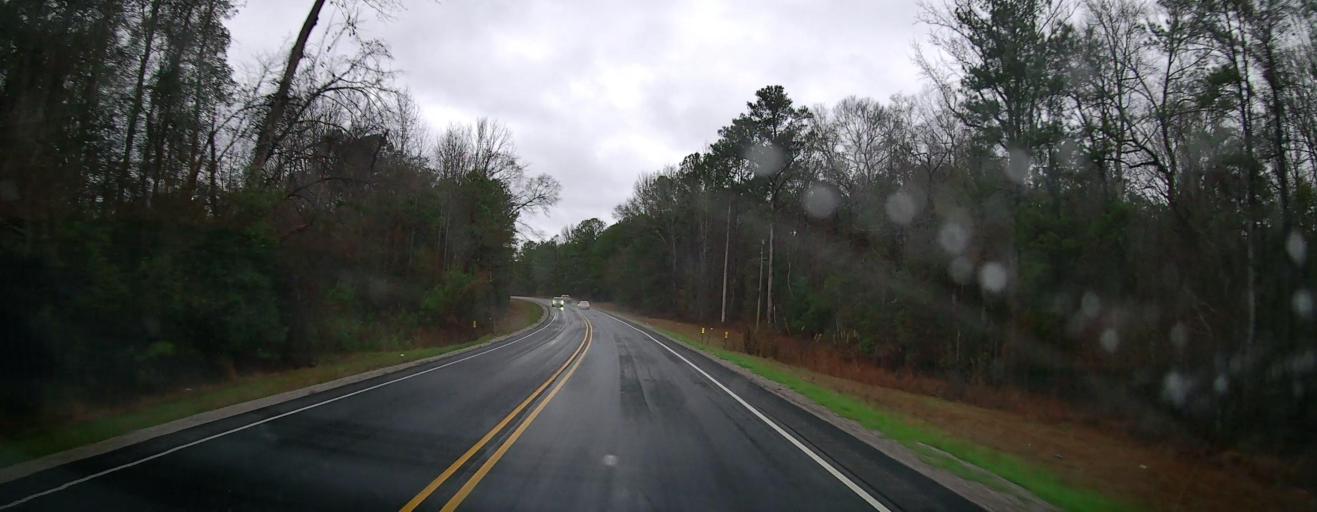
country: US
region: Alabama
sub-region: Chilton County
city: Clanton
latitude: 32.6098
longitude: -86.7174
